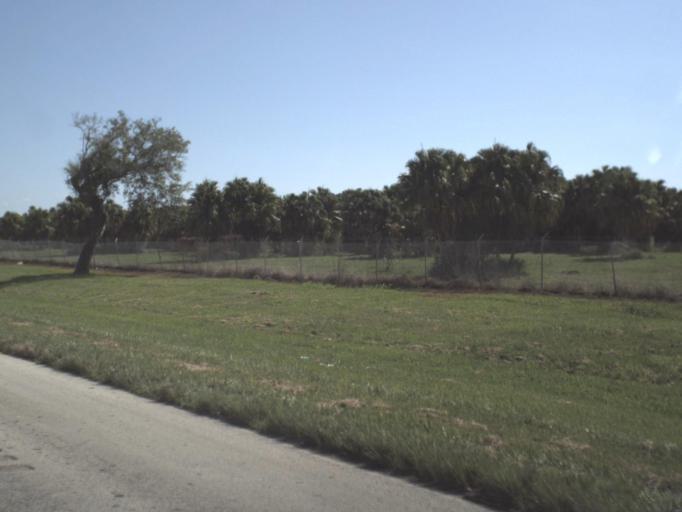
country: US
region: Florida
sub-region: Miami-Dade County
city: Princeton
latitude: 25.5298
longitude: -80.3848
